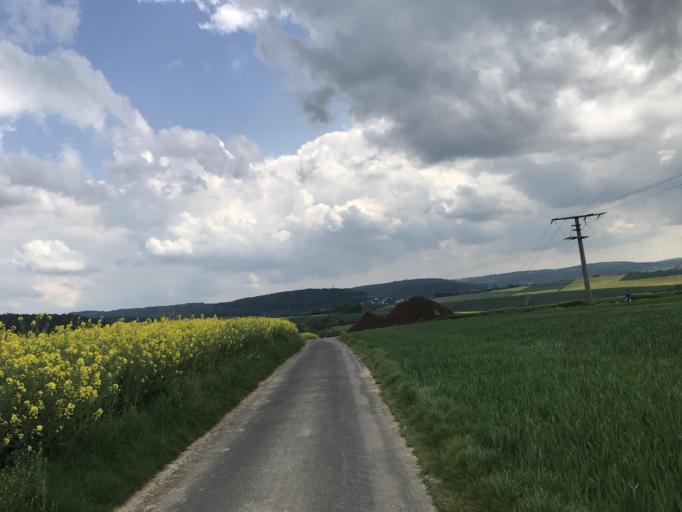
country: DE
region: Hesse
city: Budingen
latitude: 50.3105
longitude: 9.0780
